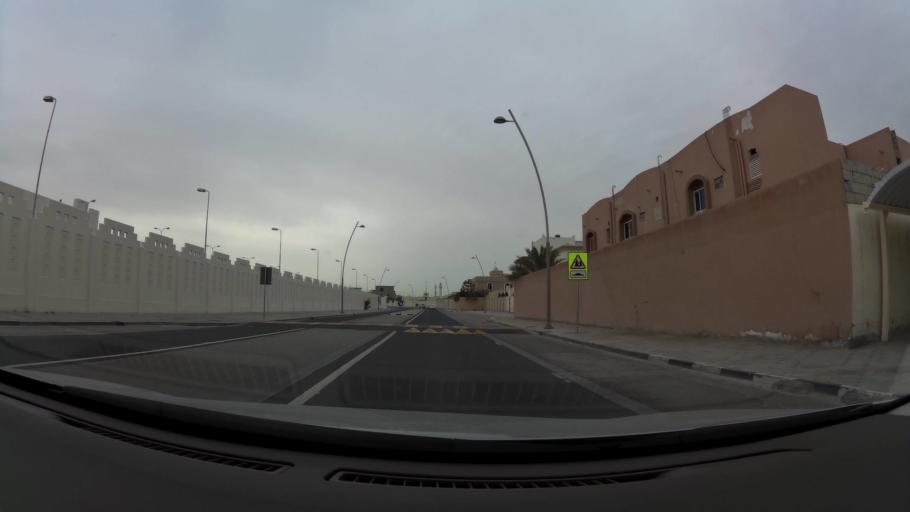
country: QA
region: Baladiyat ad Dawhah
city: Doha
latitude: 25.3461
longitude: 51.4958
